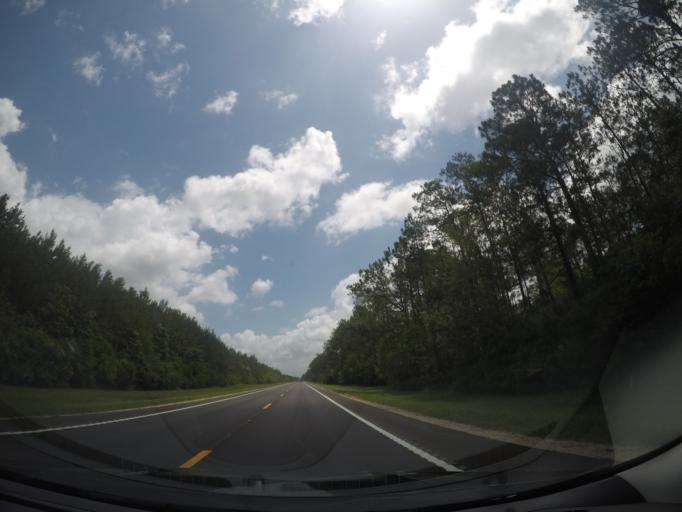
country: US
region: Mississippi
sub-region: Hancock County
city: Pearlington
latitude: 30.2859
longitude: -89.5296
